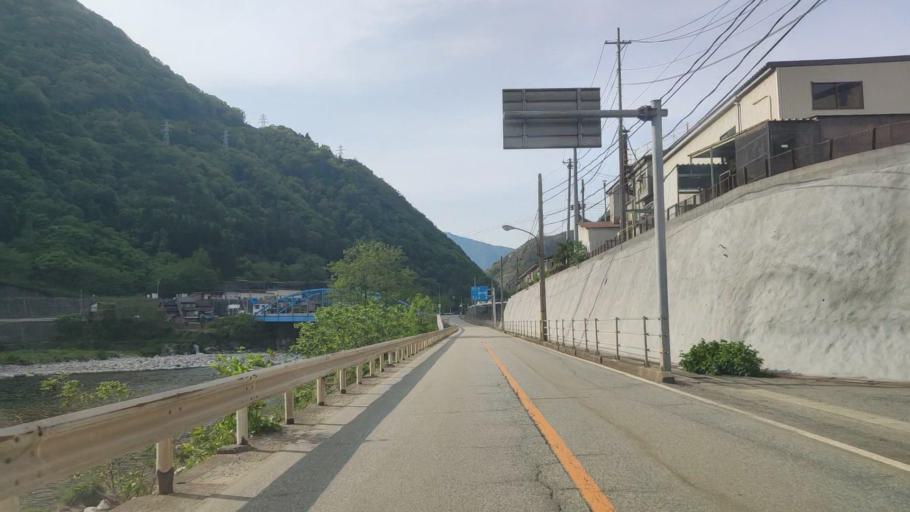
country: JP
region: Gifu
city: Takayama
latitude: 36.3382
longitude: 137.2976
